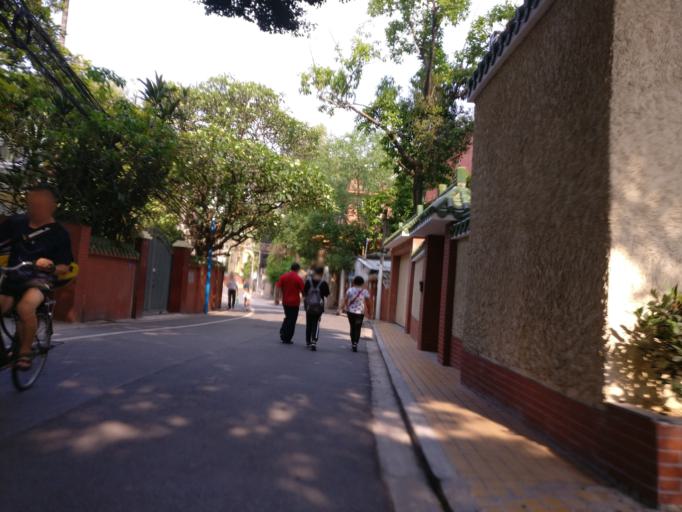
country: CN
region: Guangdong
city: Guangzhou
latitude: 23.1244
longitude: 113.2948
